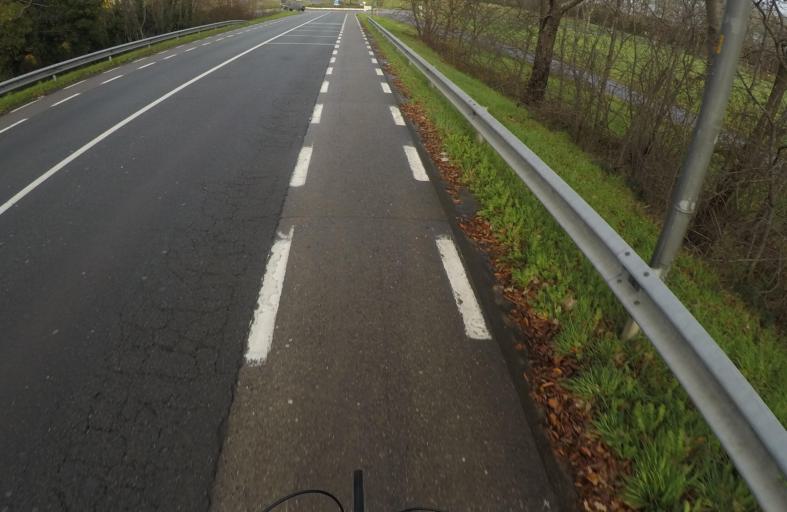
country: BE
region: Flanders
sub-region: Provincie Antwerpen
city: Wommelgem
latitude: 51.2134
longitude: 4.5276
